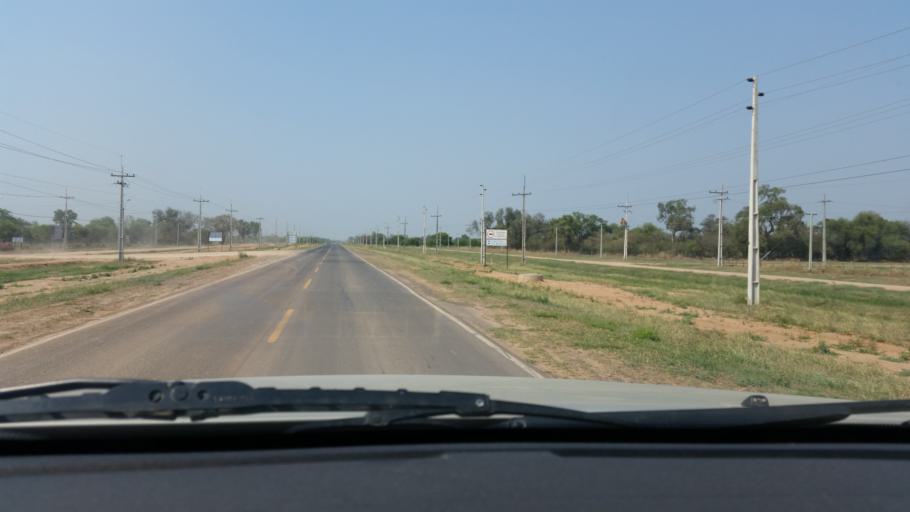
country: PY
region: Boqueron
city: Filadelfia
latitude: -22.3876
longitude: -60.0351
